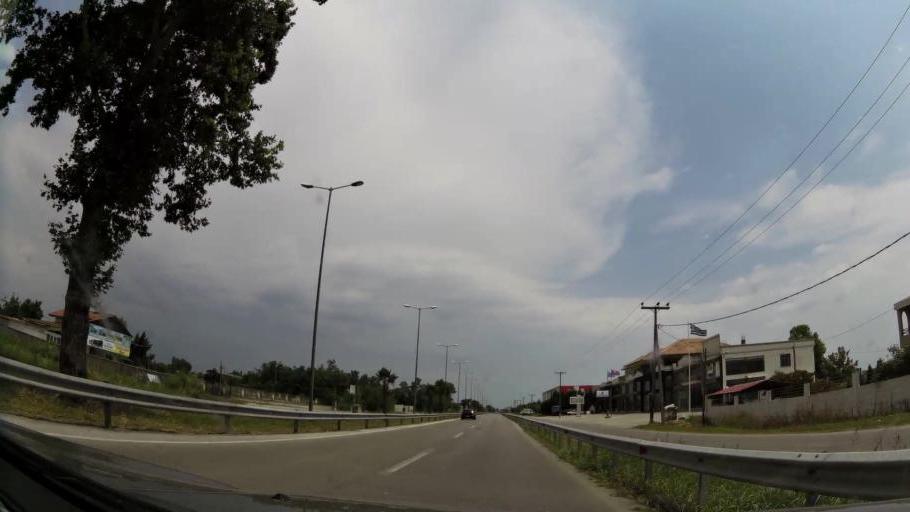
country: GR
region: Central Macedonia
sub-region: Nomos Pierias
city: Kallithea
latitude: 40.2717
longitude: 22.5624
